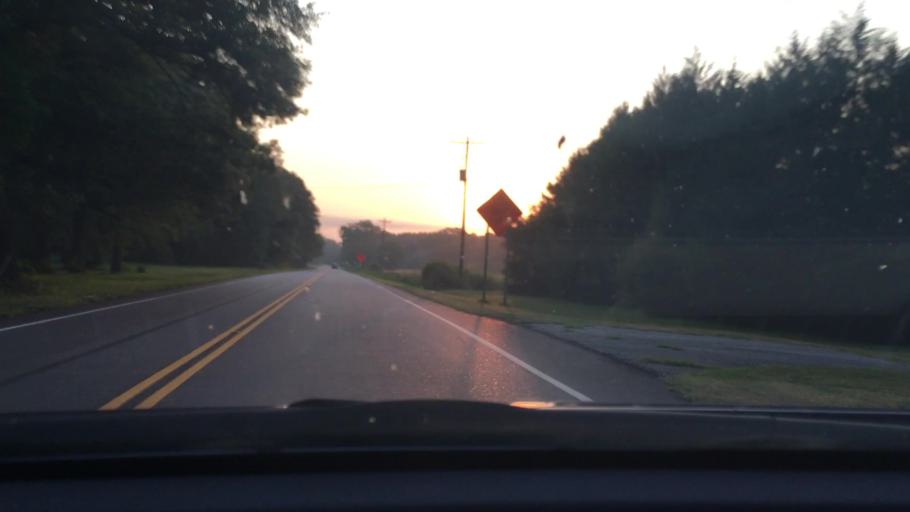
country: US
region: South Carolina
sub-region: Lee County
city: Bishopville
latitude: 34.2686
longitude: -80.1376
